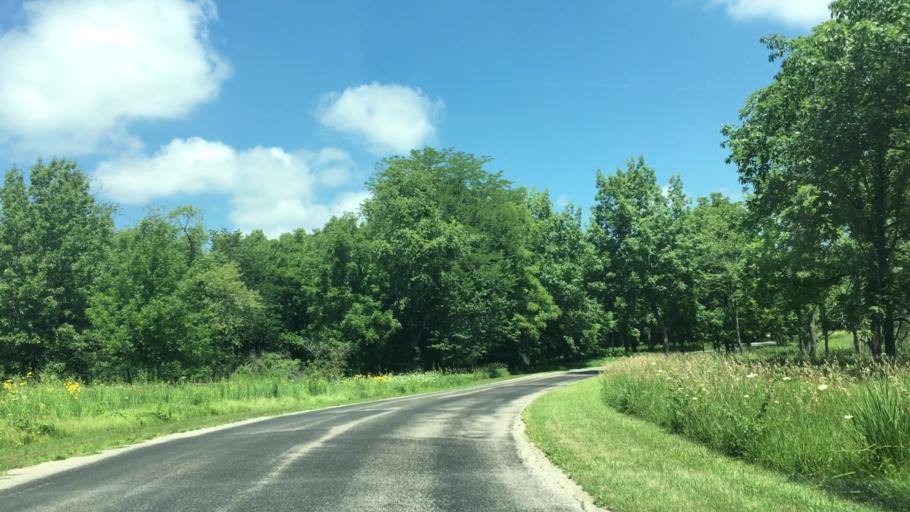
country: US
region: Iowa
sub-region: Johnson County
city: Tiffin
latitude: 41.7234
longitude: -91.7248
